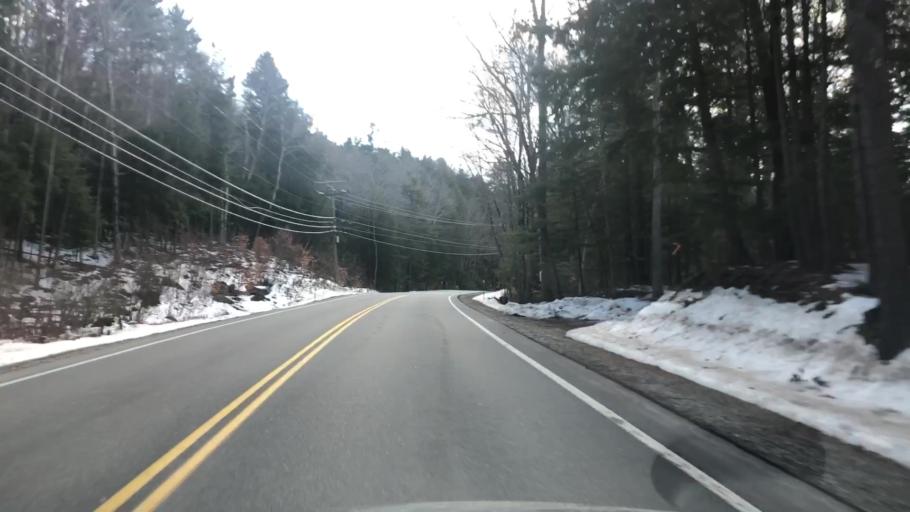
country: US
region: New Hampshire
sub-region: Hillsborough County
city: Mont Vernon
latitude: 42.8732
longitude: -71.6686
